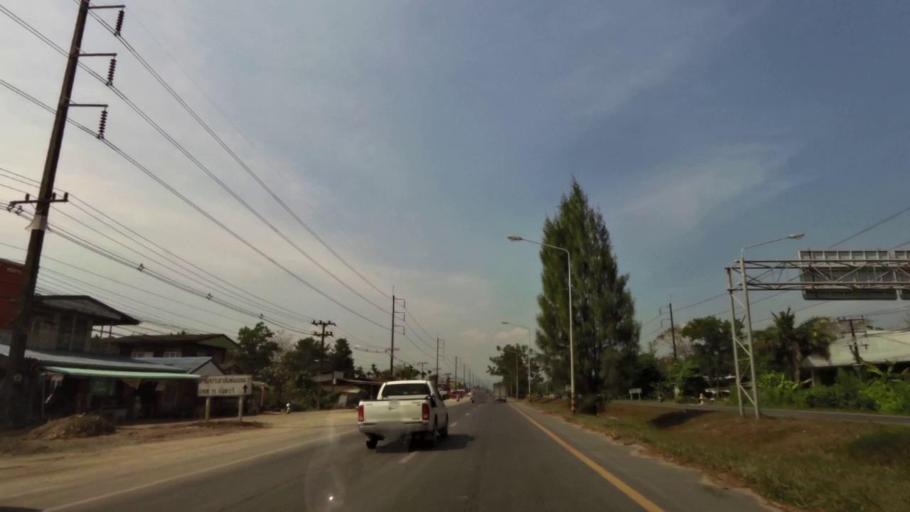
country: TH
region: Chanthaburi
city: Chanthaburi
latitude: 12.6271
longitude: 102.1484
